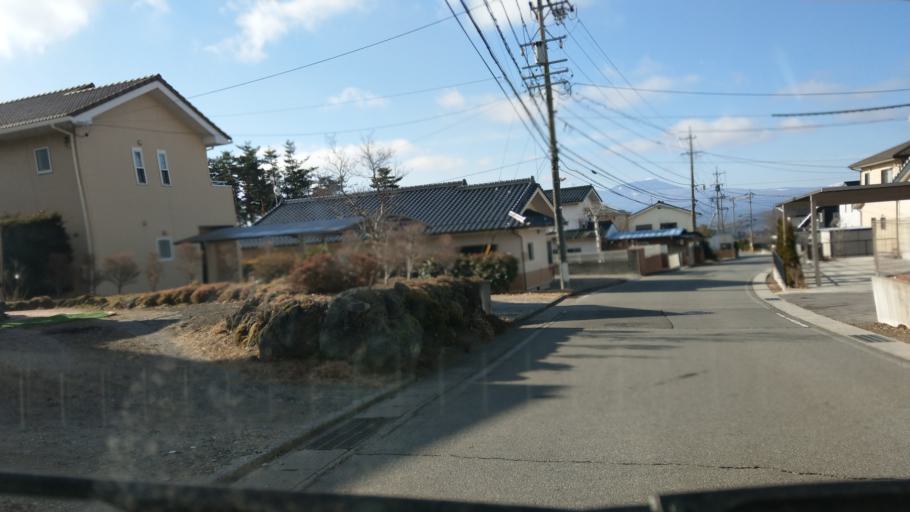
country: JP
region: Nagano
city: Komoro
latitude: 36.3260
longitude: 138.4463
